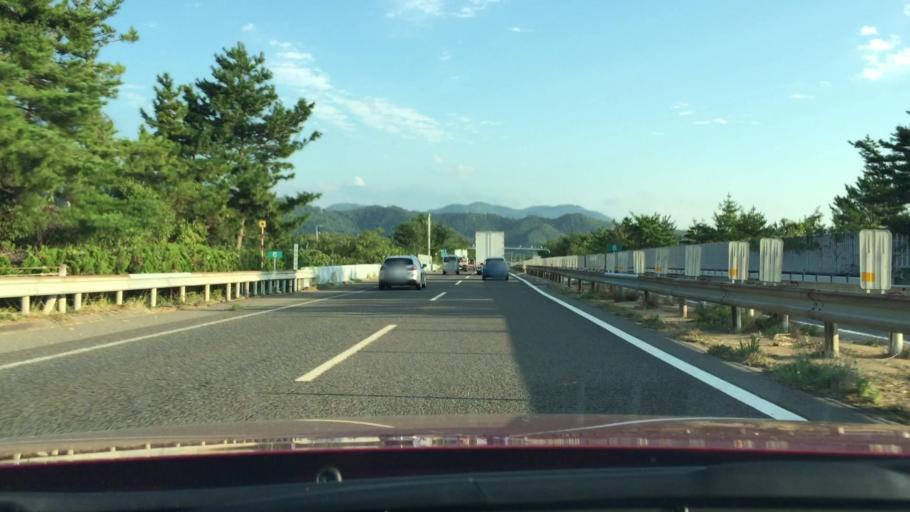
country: JP
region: Shiga Prefecture
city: Nagahama
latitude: 35.3688
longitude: 136.3050
